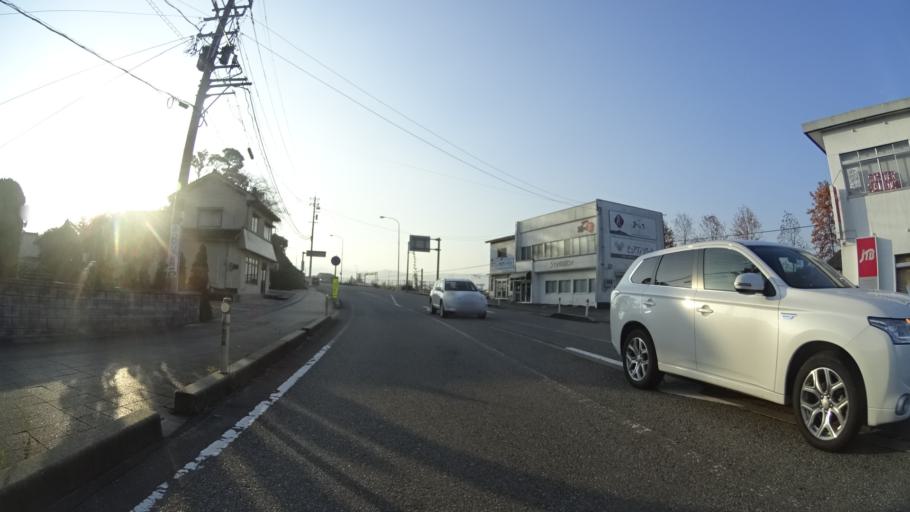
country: JP
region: Ishikawa
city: Nanao
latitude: 37.0478
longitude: 136.9575
